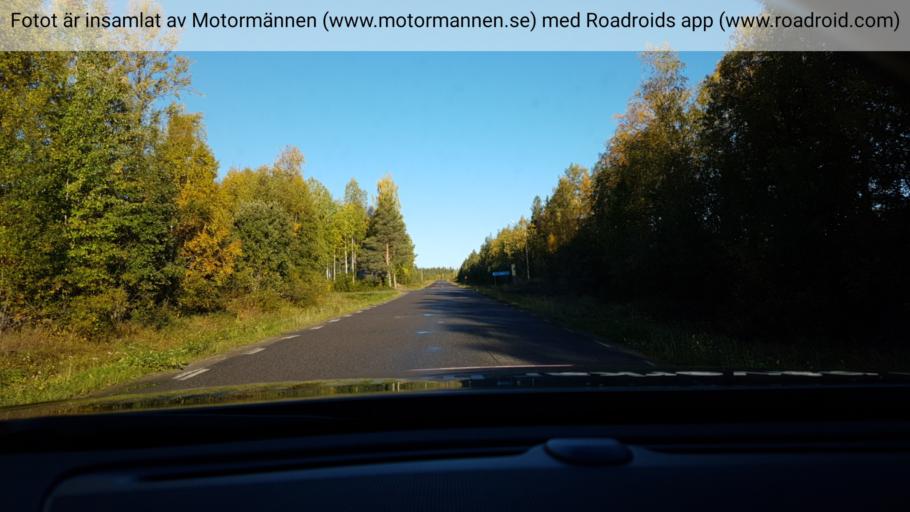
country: SE
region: Norrbotten
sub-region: Bodens Kommun
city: Boden
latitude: 66.0629
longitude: 21.4085
